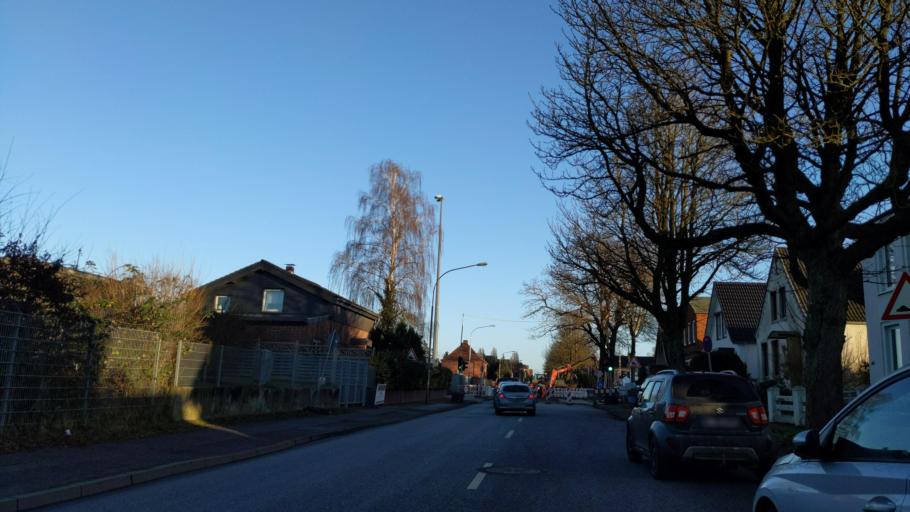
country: DE
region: Mecklenburg-Vorpommern
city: Selmsdorf
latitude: 53.8882
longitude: 10.7827
